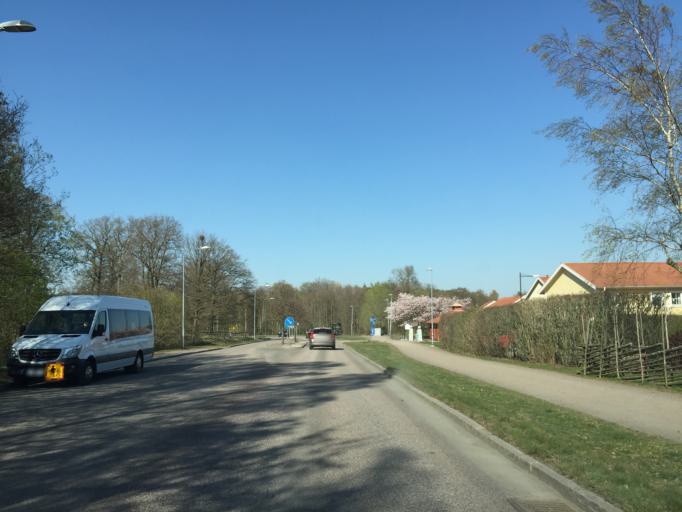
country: SE
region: Vaestra Goetaland
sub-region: Ale Kommun
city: Surte
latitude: 57.8071
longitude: 11.9757
